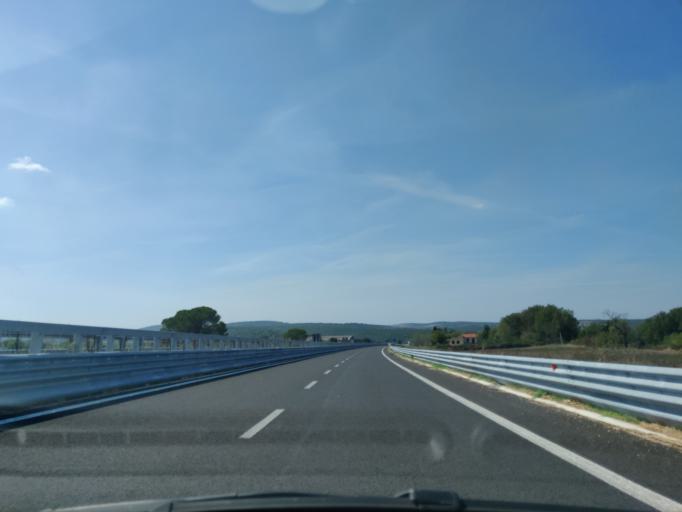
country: IT
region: Latium
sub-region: Provincia di Viterbo
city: Blera
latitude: 42.3033
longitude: 11.9844
